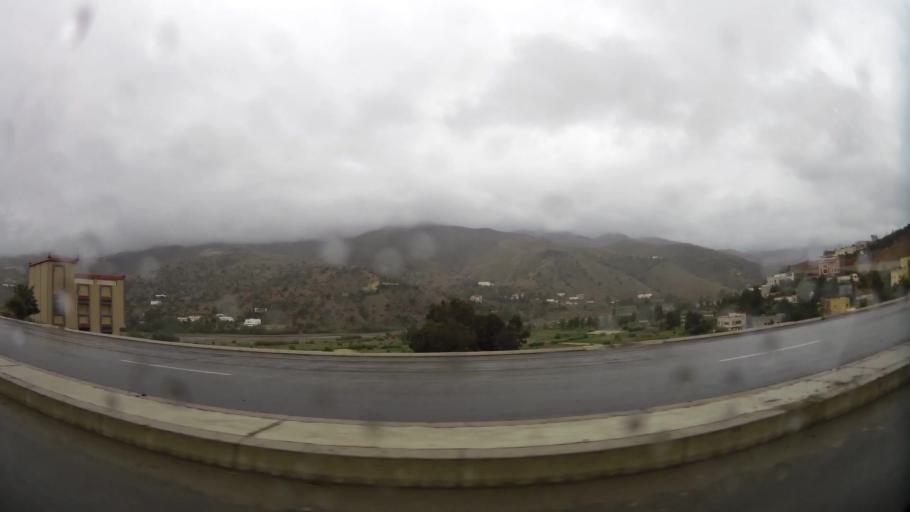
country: MA
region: Taza-Al Hoceima-Taounate
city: Imzourene
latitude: 35.0251
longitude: -3.8225
